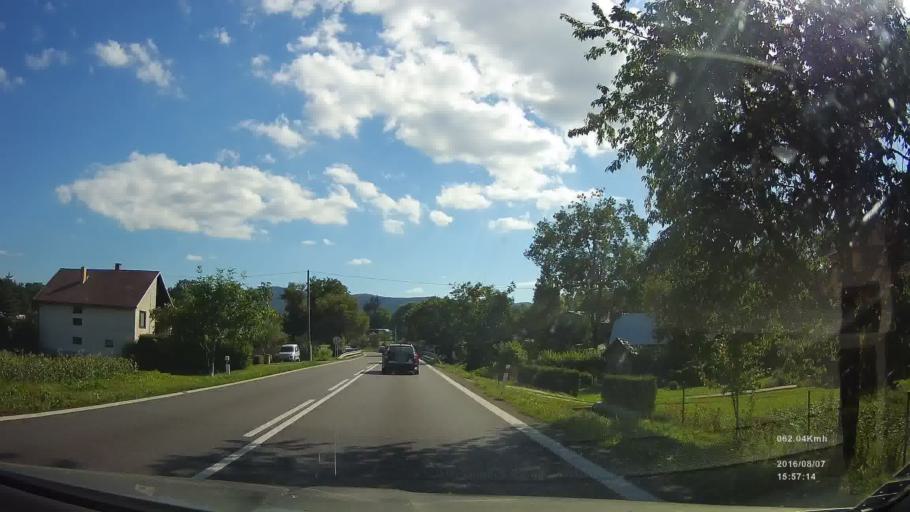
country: SK
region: Presovsky
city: Giraltovce
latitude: 49.0609
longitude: 21.4175
